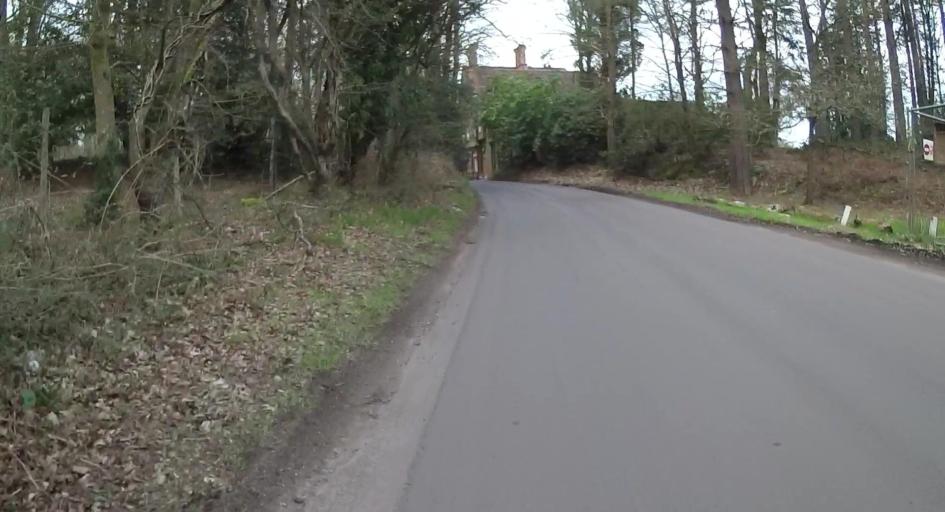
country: GB
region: England
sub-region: Hampshire
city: Lindford
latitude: 51.1395
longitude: -0.8381
